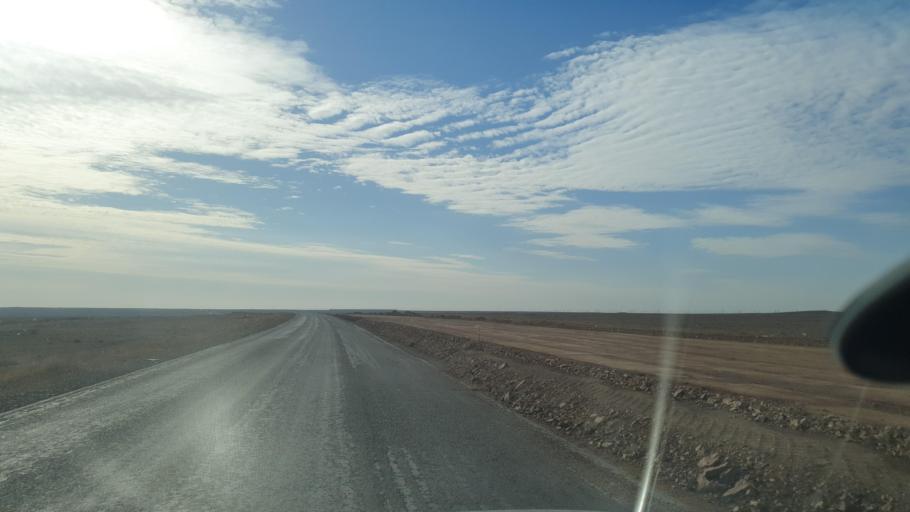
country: KZ
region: Qaraghandy
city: Saryshaghan
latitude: 45.9710
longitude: 73.5495
